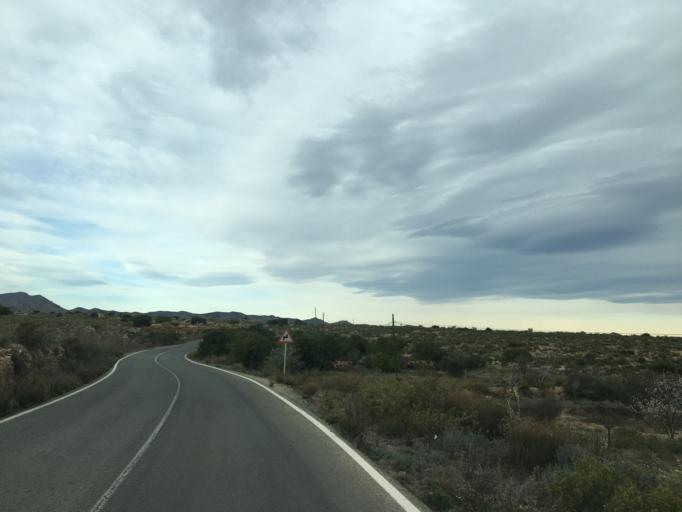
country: ES
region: Murcia
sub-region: Murcia
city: Cartagena
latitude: 37.6160
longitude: -1.0660
